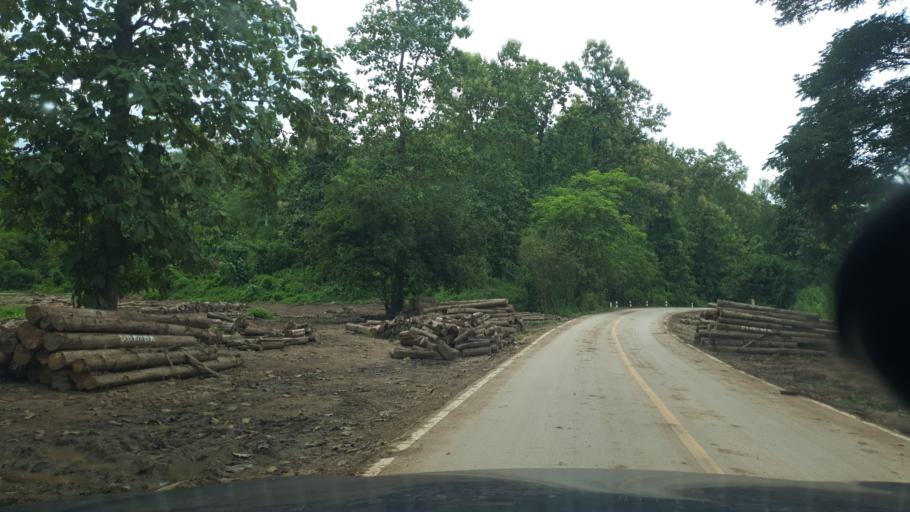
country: TH
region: Lampang
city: Hang Chat
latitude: 18.3744
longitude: 99.2596
